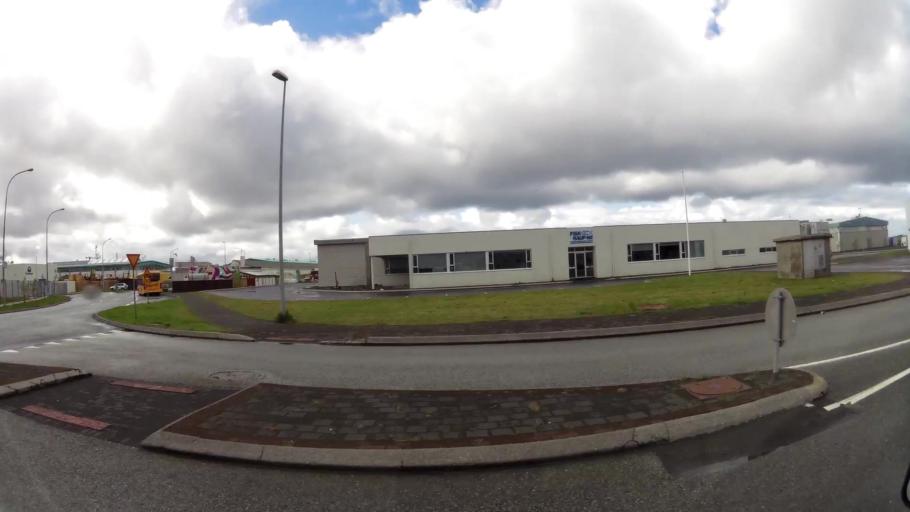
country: IS
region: Capital Region
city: Reykjavik
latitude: 64.1564
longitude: -21.9411
